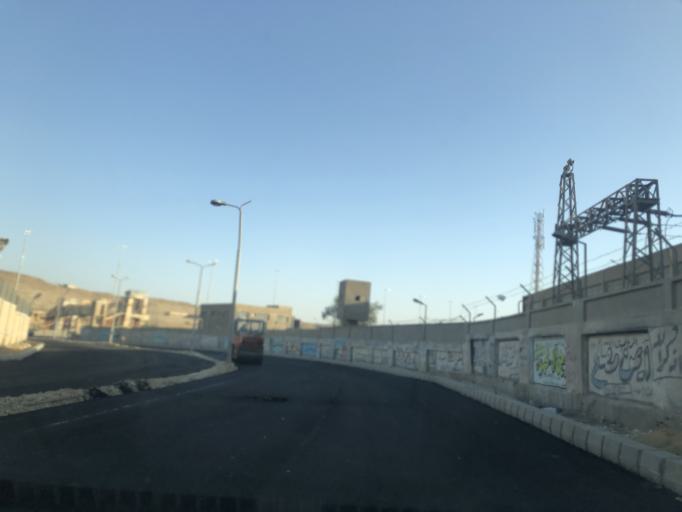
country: EG
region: Al Jizah
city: Al Jizah
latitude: 29.9800
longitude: 31.1129
